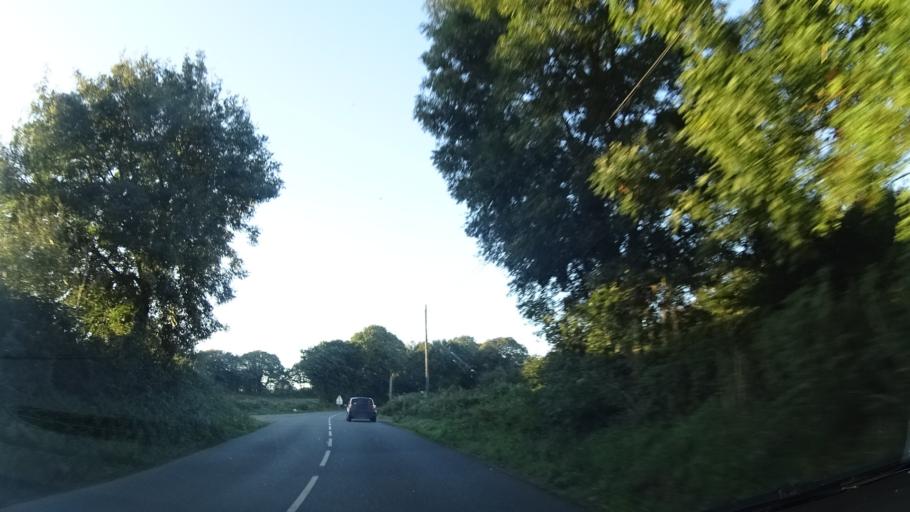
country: FR
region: Brittany
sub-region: Departement du Finistere
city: Guilers
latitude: 48.4070
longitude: -4.5517
